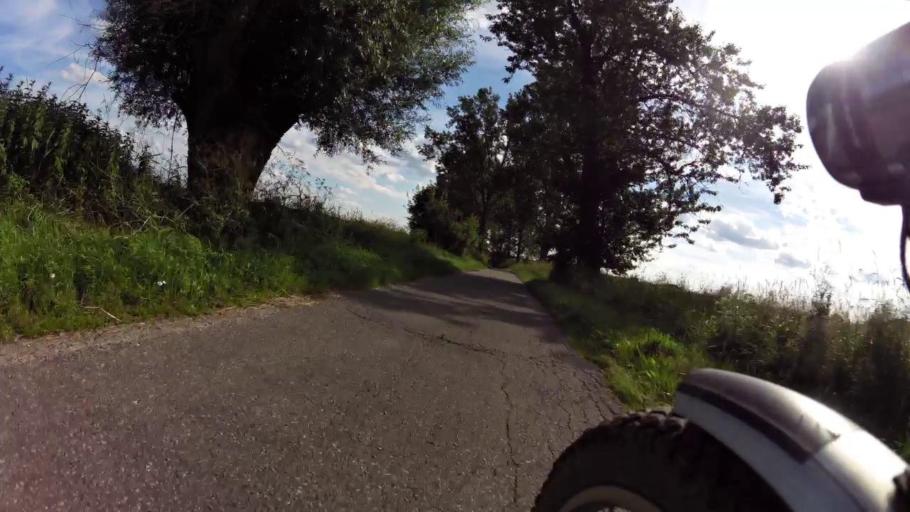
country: PL
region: West Pomeranian Voivodeship
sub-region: Powiat lobeski
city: Radowo Male
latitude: 53.5794
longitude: 15.4703
